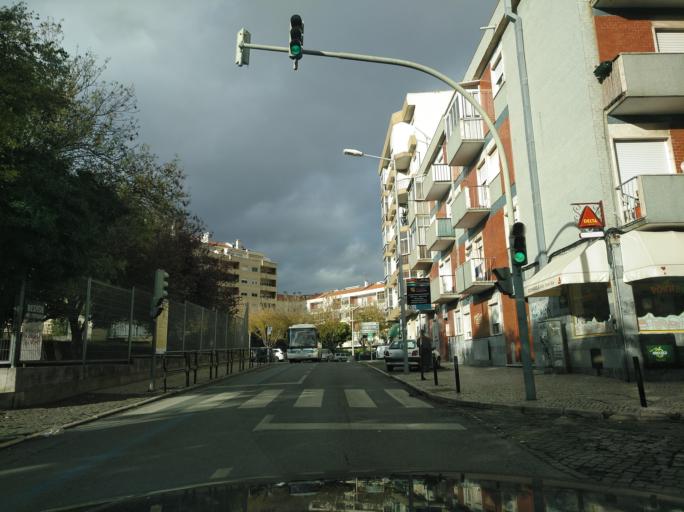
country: PT
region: Lisbon
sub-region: Loures
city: Sacavem
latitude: 38.7919
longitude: -9.1106
